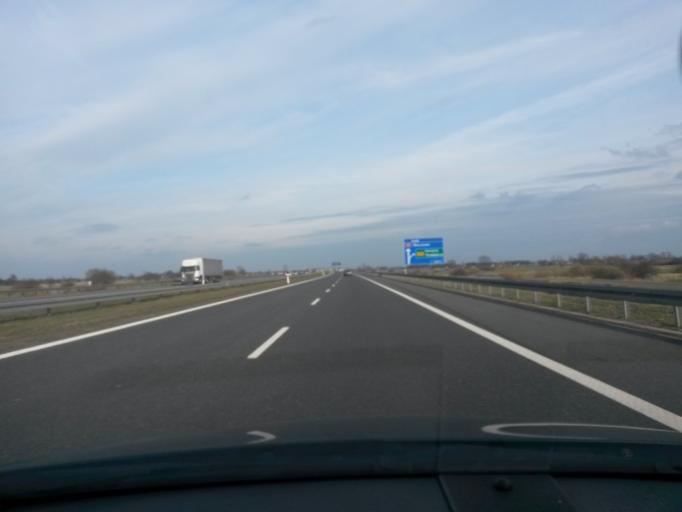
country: PL
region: Lodz Voivodeship
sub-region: Powiat poddebicki
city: Wartkowice
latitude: 51.9991
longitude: 19.0099
